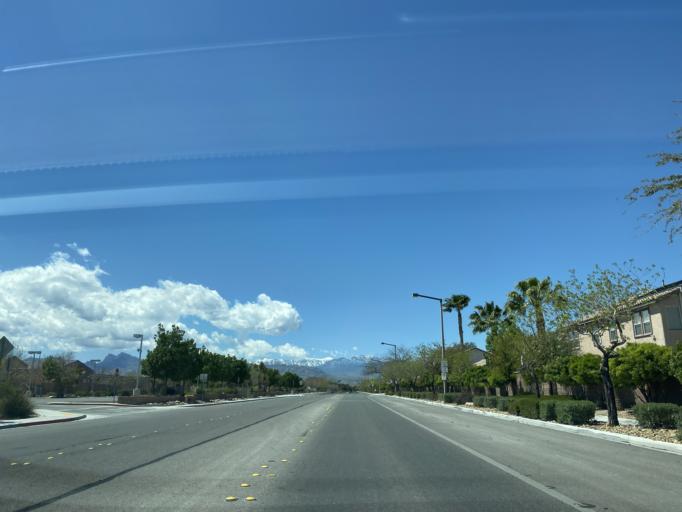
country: US
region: Nevada
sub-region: Clark County
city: North Las Vegas
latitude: 36.3130
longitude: -115.2164
